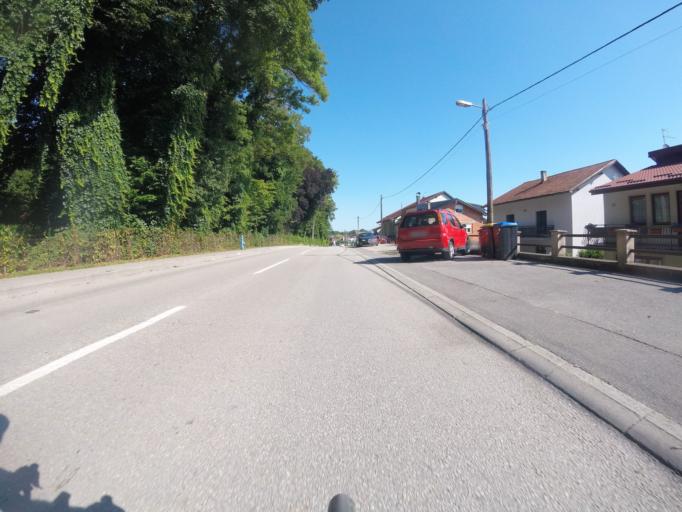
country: HR
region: Zagrebacka
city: Bregana
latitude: 45.8223
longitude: 15.6986
